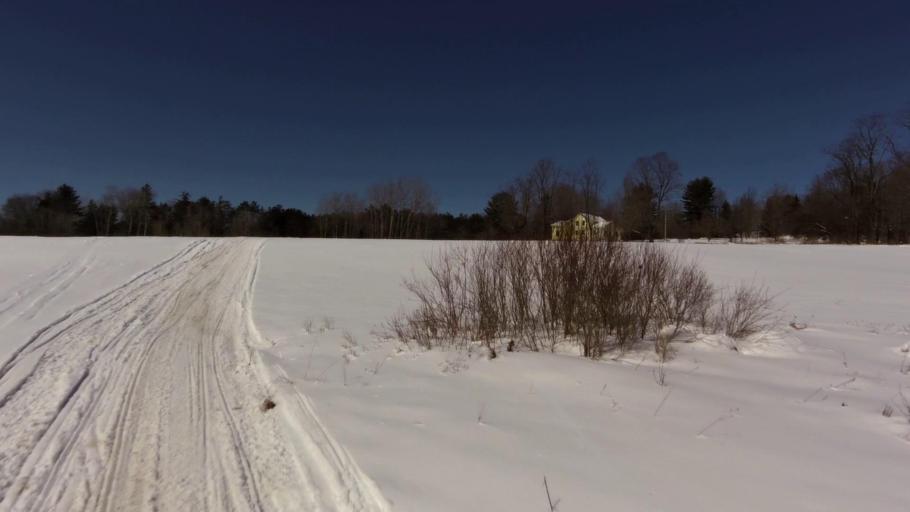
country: US
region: New York
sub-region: Allegany County
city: Cuba
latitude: 42.3387
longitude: -78.2506
